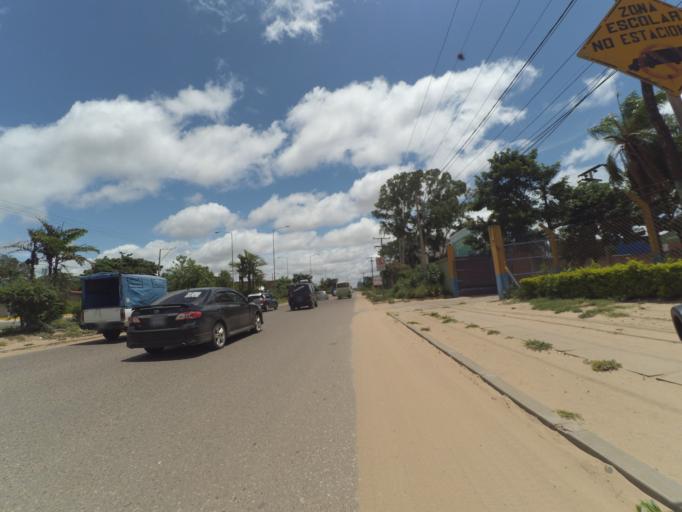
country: BO
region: Santa Cruz
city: Santa Cruz de la Sierra
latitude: -17.8370
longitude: -63.2365
